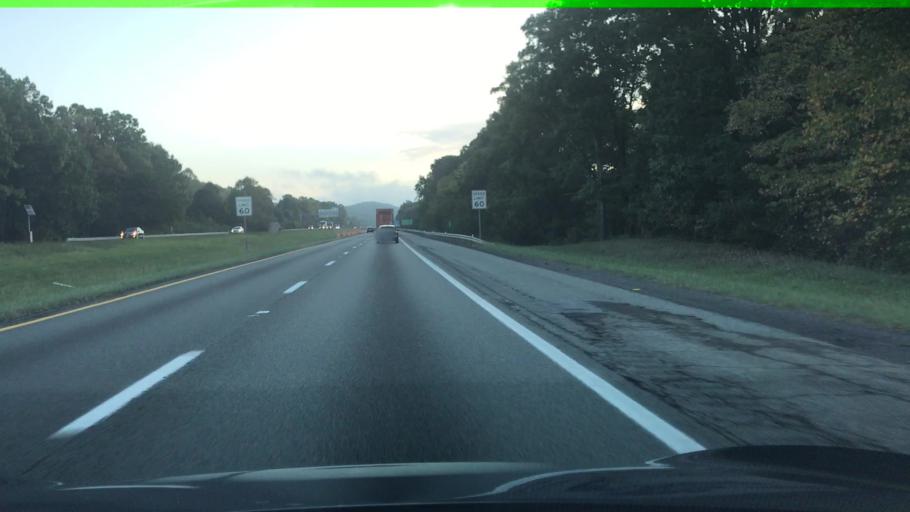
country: US
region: Virginia
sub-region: Roanoke County
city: Hollins
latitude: 37.3473
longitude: -79.9891
